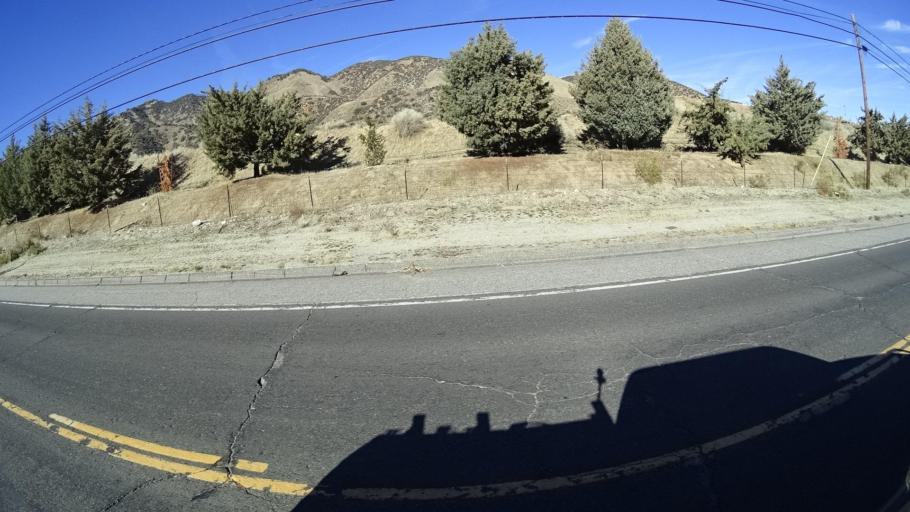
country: US
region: California
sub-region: Kern County
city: Frazier Park
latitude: 34.8171
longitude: -118.9030
